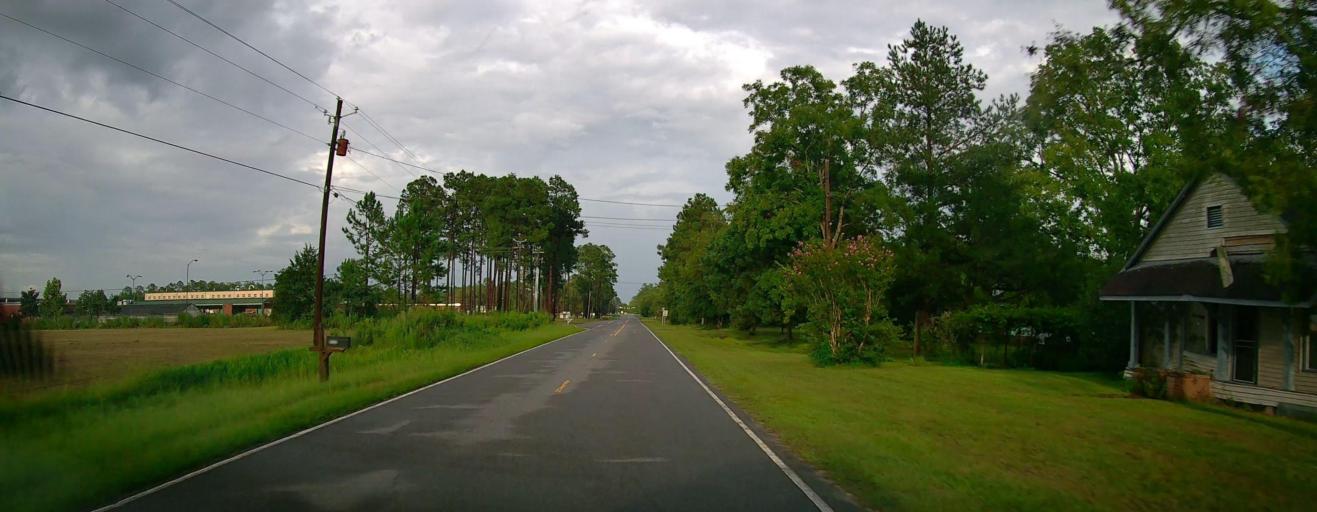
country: US
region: Georgia
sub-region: Ware County
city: Deenwood
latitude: 31.1951
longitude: -82.3911
